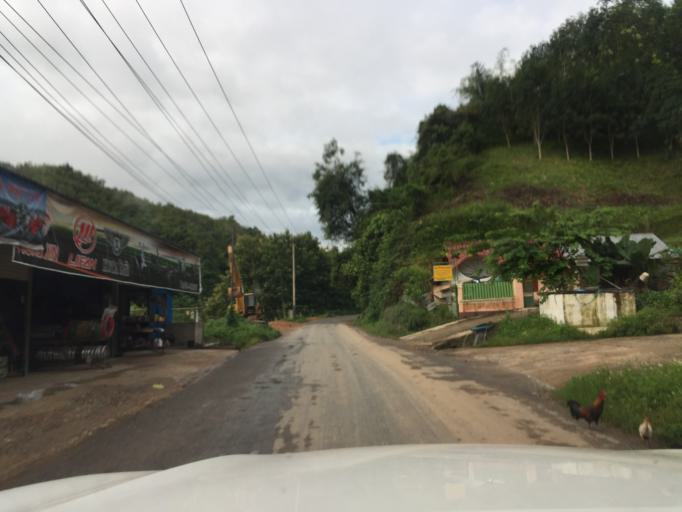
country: LA
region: Phongsali
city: Khoa
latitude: 21.0964
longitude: 102.2505
